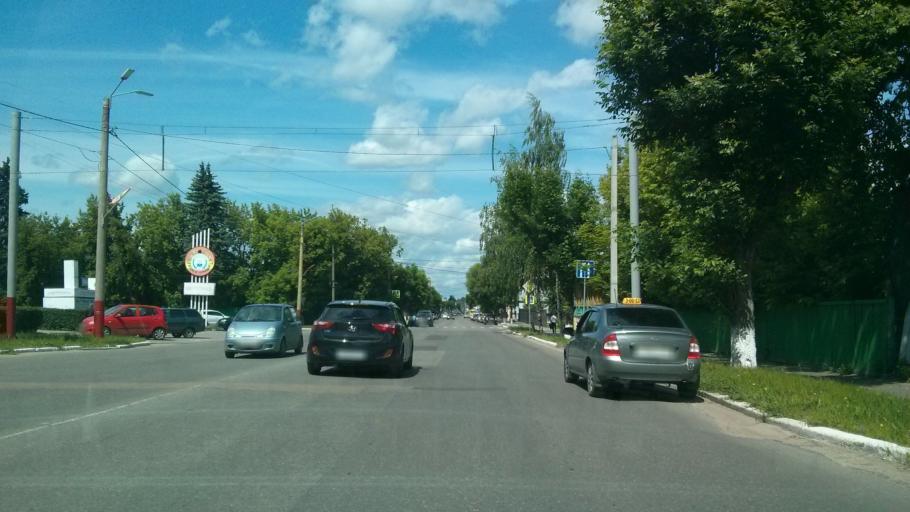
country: RU
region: Vladimir
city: Murom
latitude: 55.5747
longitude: 42.0557
